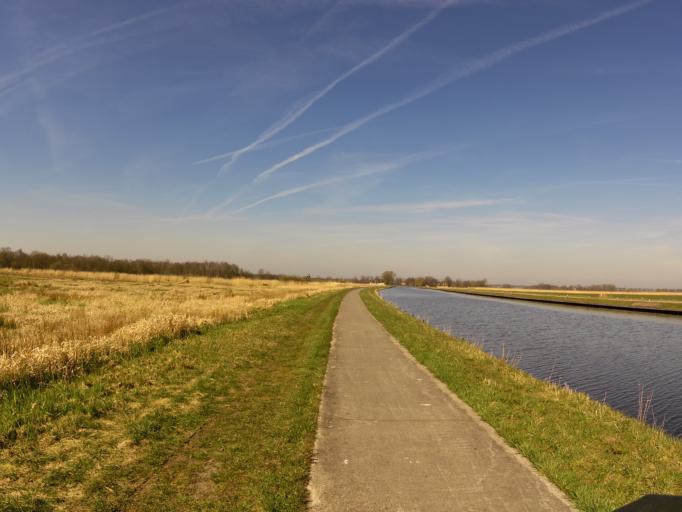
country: NL
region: Overijssel
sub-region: Gemeente Steenwijkerland
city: Oldemarkt
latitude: 52.8039
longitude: 5.9483
